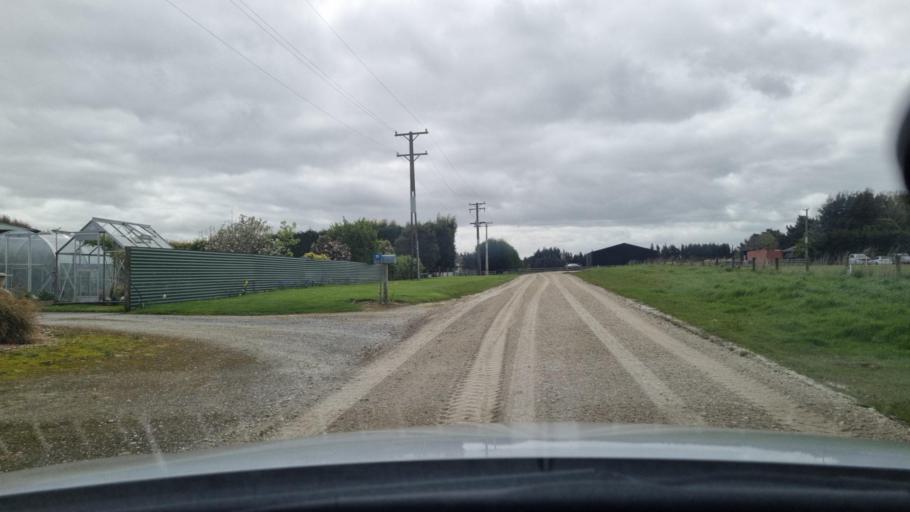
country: NZ
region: Southland
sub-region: Invercargill City
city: Invercargill
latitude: -46.4331
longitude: 168.4097
